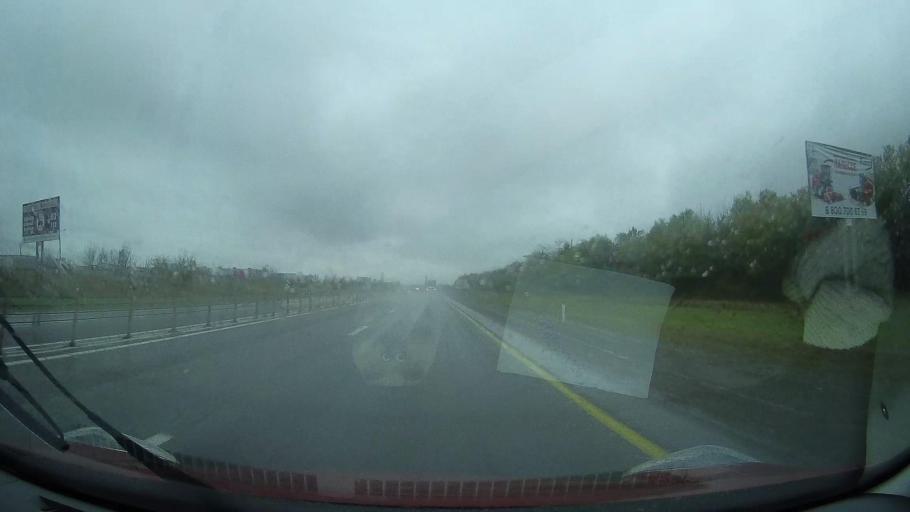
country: RU
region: Stavropol'skiy
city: Nevinnomyssk
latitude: 44.6410
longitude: 41.9670
